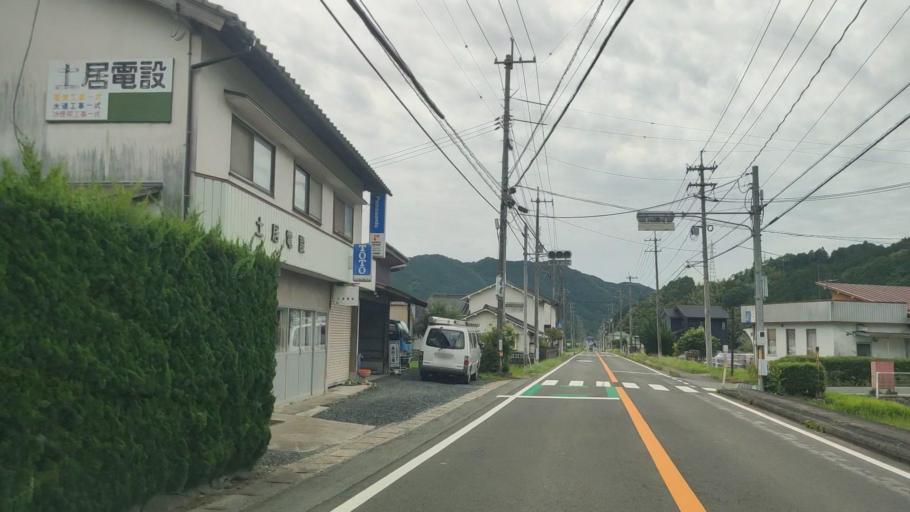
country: JP
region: Hyogo
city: Yamazakicho-nakabirose
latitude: 35.1033
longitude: 134.3253
